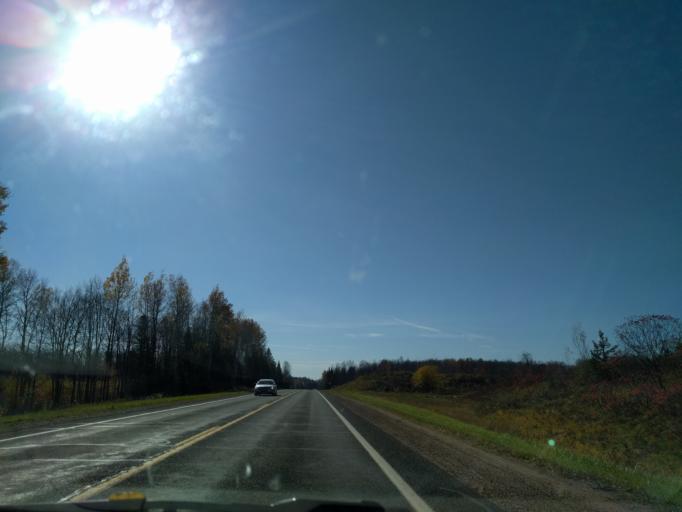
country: US
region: Michigan
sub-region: Iron County
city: Crystal Falls
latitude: 46.1834
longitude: -88.0407
